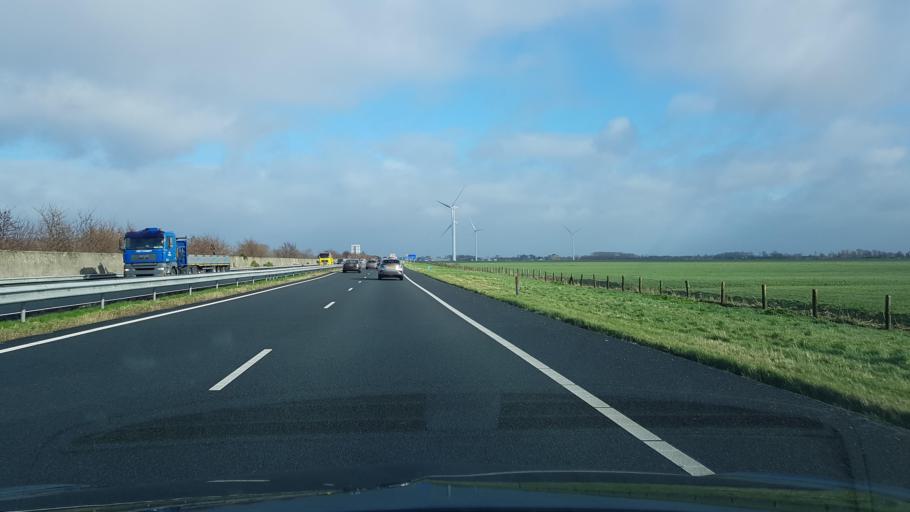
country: NL
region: South Holland
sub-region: Gemeente Alphen aan den Rijn
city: Alphen aan den Rijn
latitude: 52.1229
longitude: 4.5946
